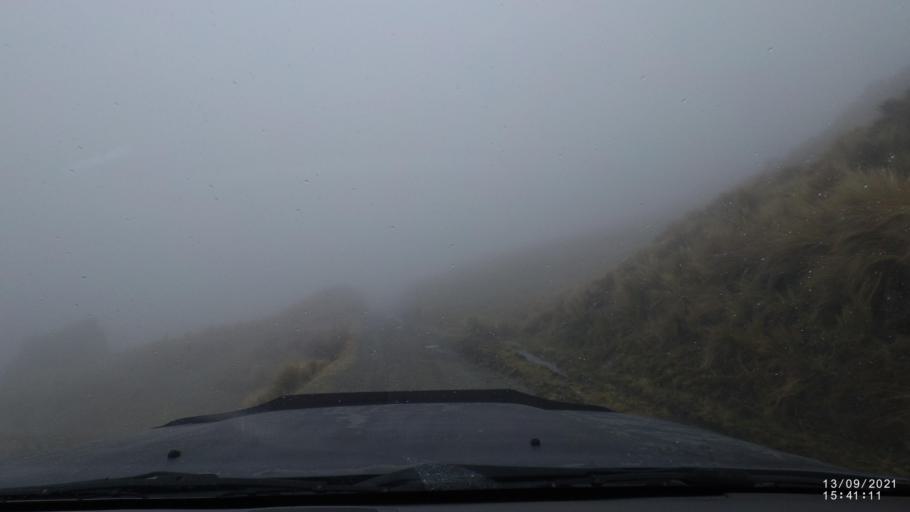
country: BO
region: Cochabamba
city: Colomi
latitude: -17.3238
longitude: -65.7179
